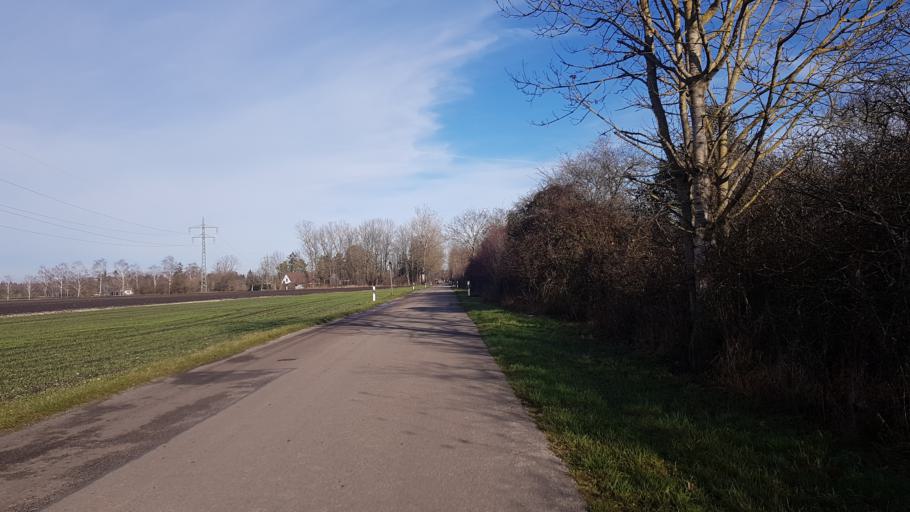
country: DE
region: Bavaria
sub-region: Upper Bavaria
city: Karlsfeld
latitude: 48.2378
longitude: 11.5058
